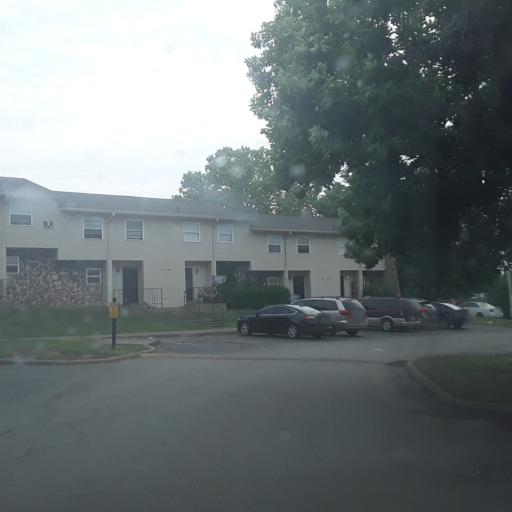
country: US
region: Tennessee
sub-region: Williamson County
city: Brentwood Estates
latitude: 36.0475
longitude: -86.7174
